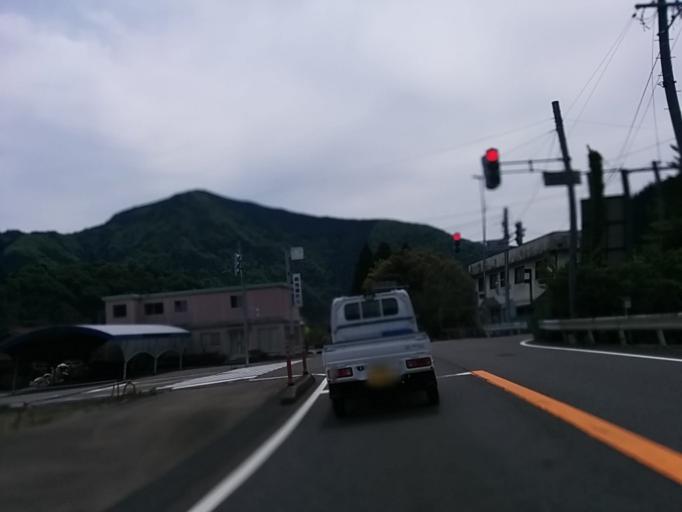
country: JP
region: Gifu
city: Gujo
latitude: 35.7385
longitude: 136.9481
